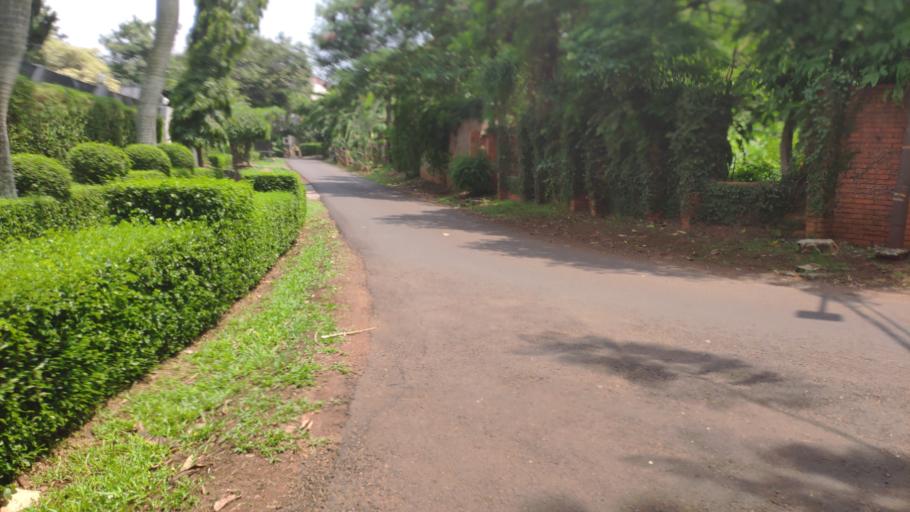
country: ID
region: Jakarta Raya
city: Jakarta
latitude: -6.2747
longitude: 106.8229
